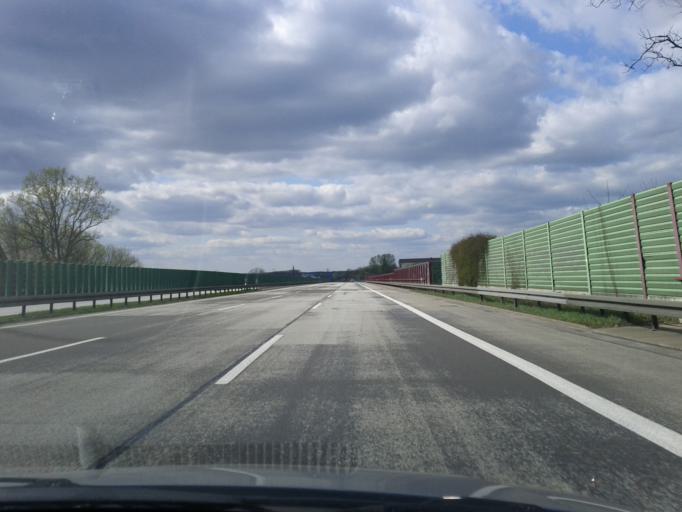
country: DE
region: Brandenburg
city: Woltersdorf
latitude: 52.4663
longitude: 13.7852
